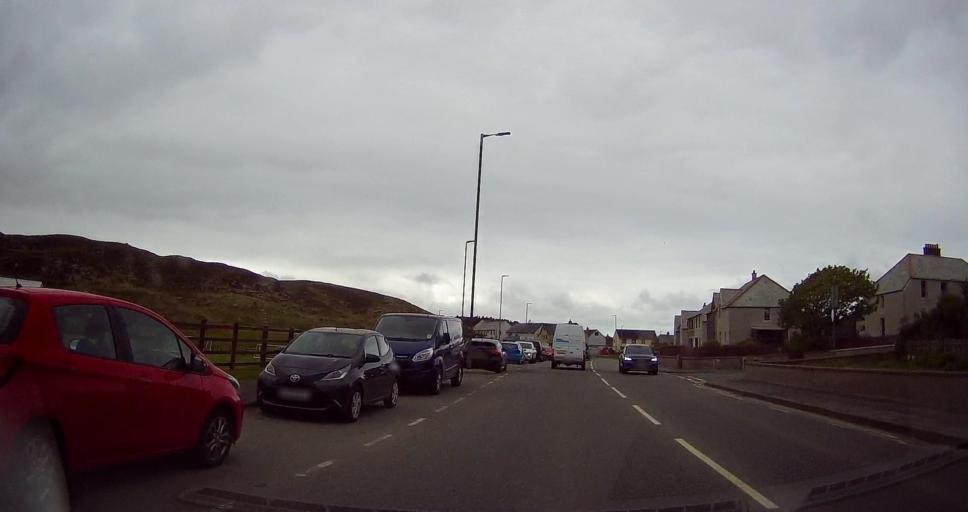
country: GB
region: Scotland
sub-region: Shetland Islands
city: Lerwick
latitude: 60.1550
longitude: -1.1598
